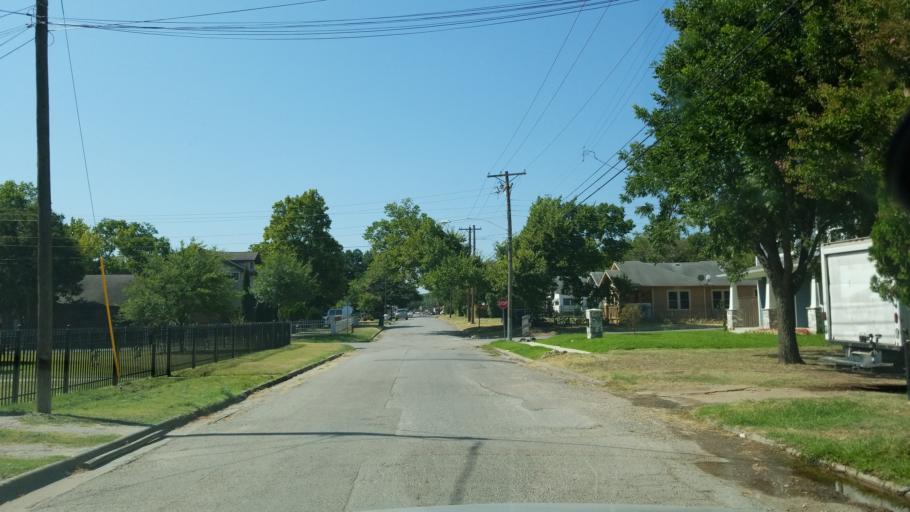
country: US
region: Texas
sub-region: Dallas County
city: Cockrell Hill
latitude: 32.7403
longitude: -96.8900
